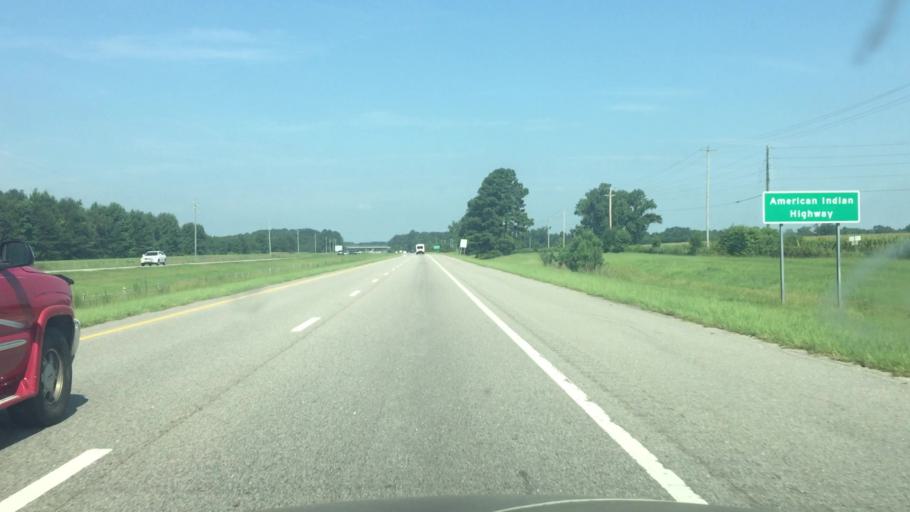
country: US
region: North Carolina
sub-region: Robeson County
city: Lumberton
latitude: 34.5842
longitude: -79.0561
